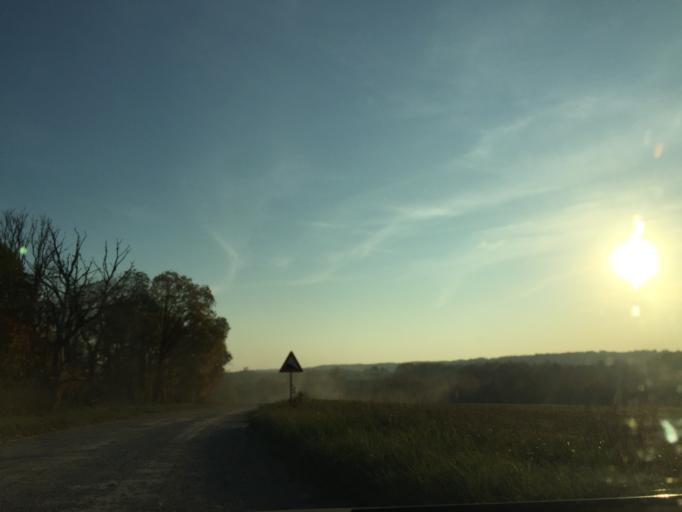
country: LV
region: Vainode
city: Vainode
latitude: 56.5308
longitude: 21.8295
